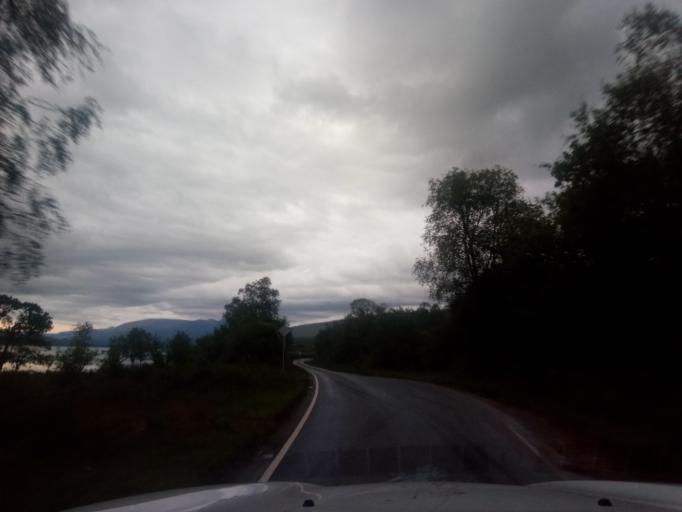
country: GB
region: Scotland
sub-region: Highland
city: Fort William
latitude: 56.8520
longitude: -5.3279
